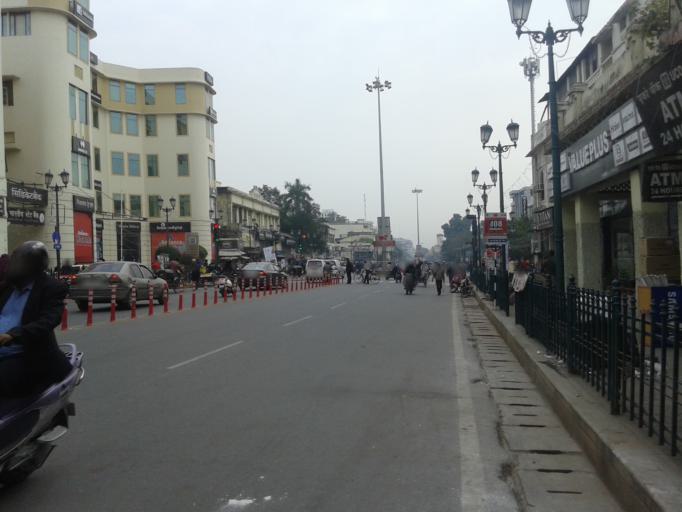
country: IN
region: Uttar Pradesh
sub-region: Lucknow District
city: Lucknow
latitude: 26.8502
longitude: 80.9412
